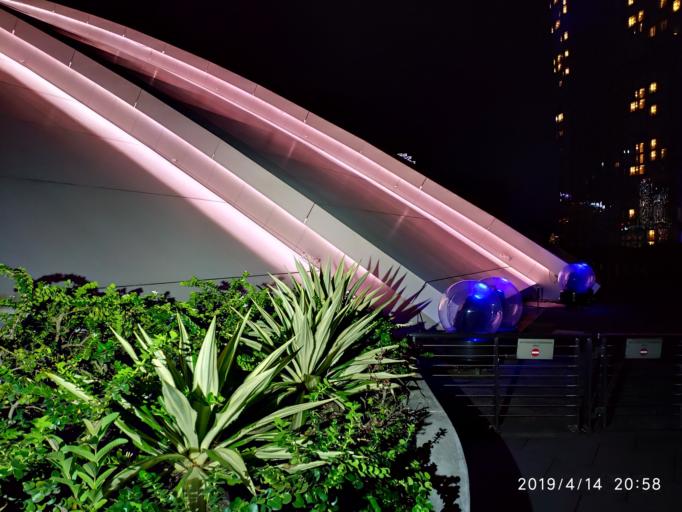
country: SG
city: Singapore
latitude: 1.2834
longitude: 103.8596
